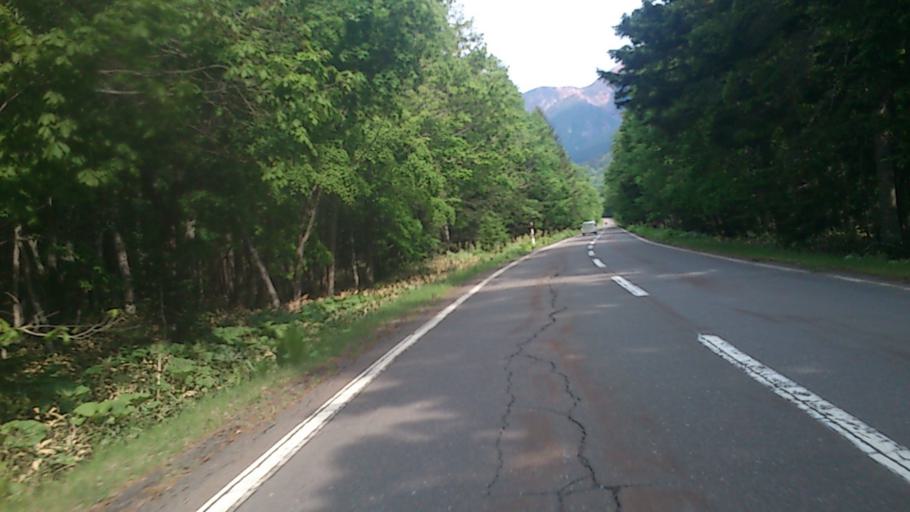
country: JP
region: Hokkaido
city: Kitami
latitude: 43.4057
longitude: 143.9584
